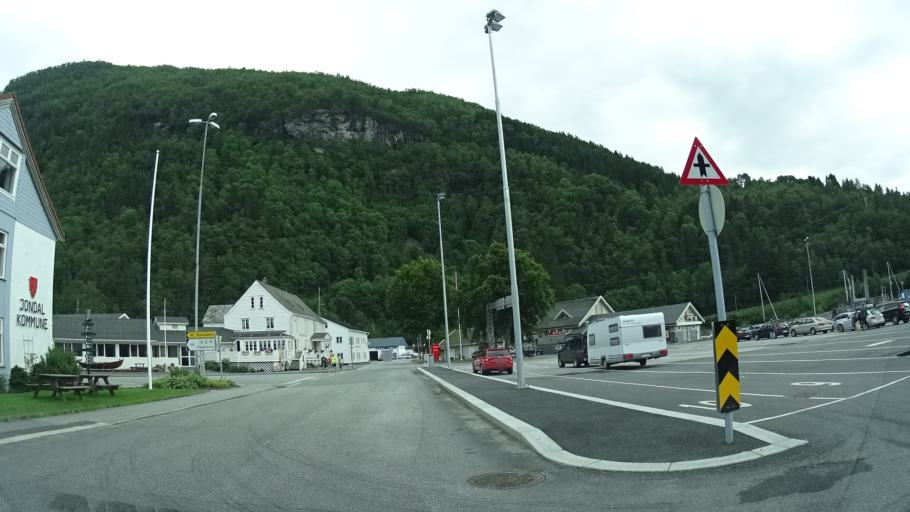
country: NO
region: Hordaland
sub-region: Jondal
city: Jondal
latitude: 60.2763
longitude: 6.2522
